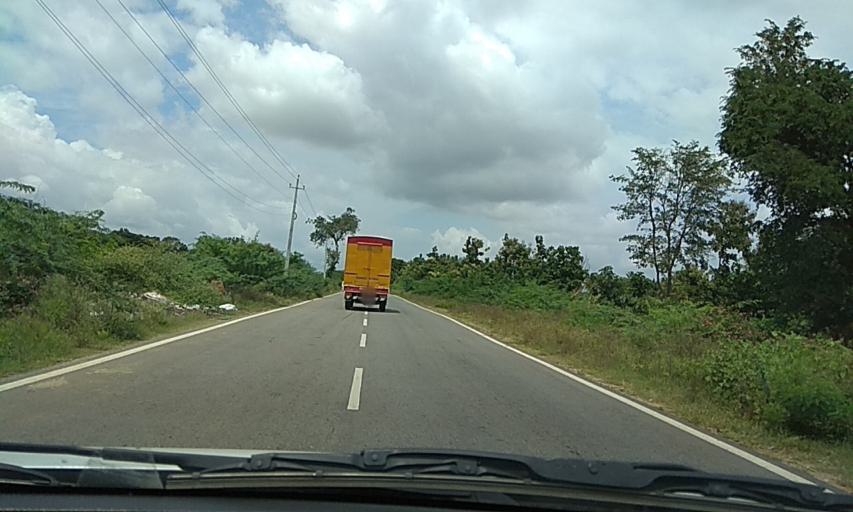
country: IN
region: Karnataka
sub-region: Chamrajnagar
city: Gundlupet
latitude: 11.8139
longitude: 76.7805
